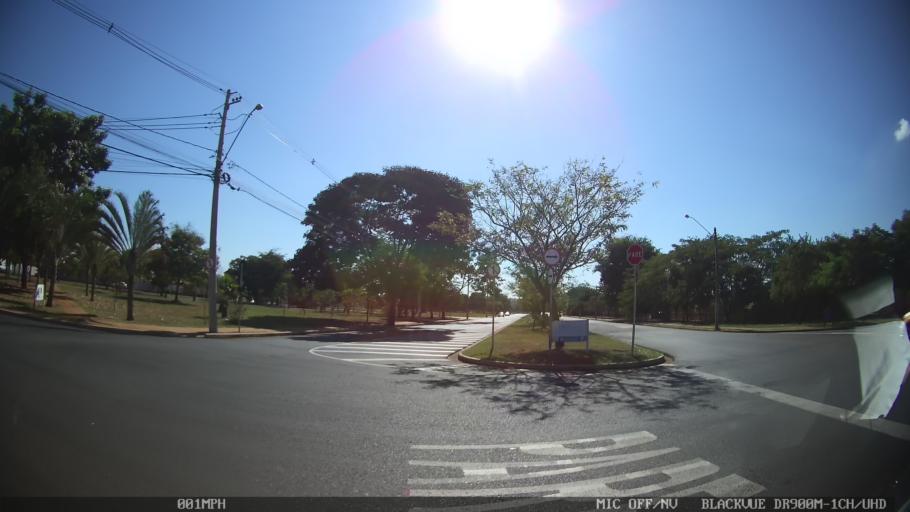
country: BR
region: Sao Paulo
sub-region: Ribeirao Preto
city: Ribeirao Preto
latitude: -21.2169
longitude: -47.7627
